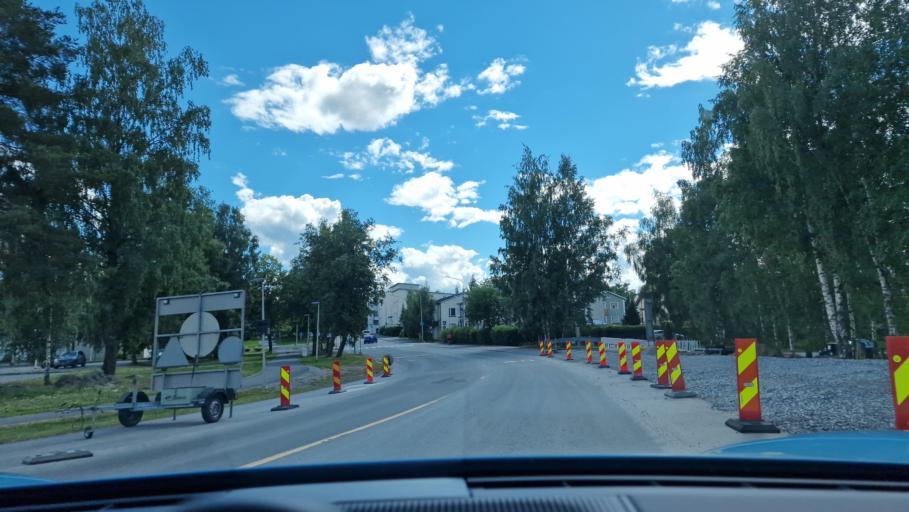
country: FI
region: Pirkanmaa
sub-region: Etelae-Pirkanmaa
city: Valkeakoski
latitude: 61.2715
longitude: 24.0289
